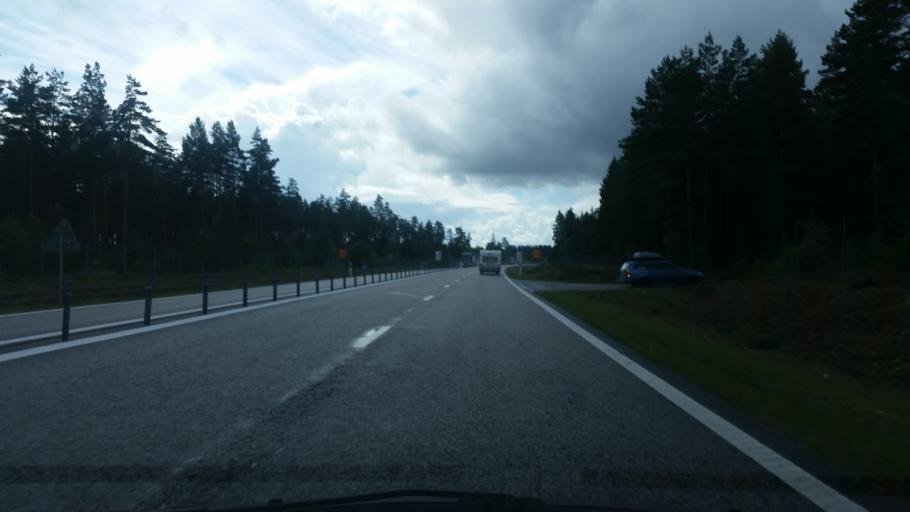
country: SE
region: Joenkoeping
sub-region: Gislaveds Kommun
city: Gislaved
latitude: 57.3502
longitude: 13.5566
